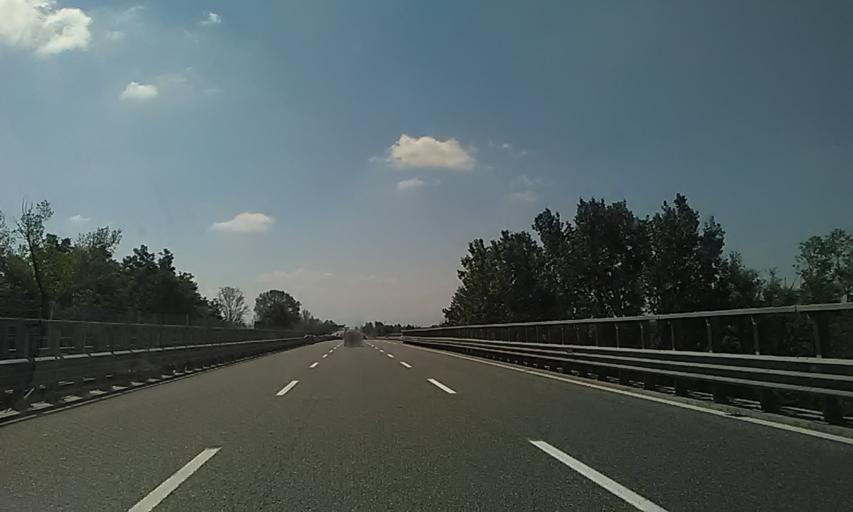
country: IT
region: Piedmont
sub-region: Provincia di Alessandria
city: Castellazzo Bormida
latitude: 44.8602
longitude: 8.5835
